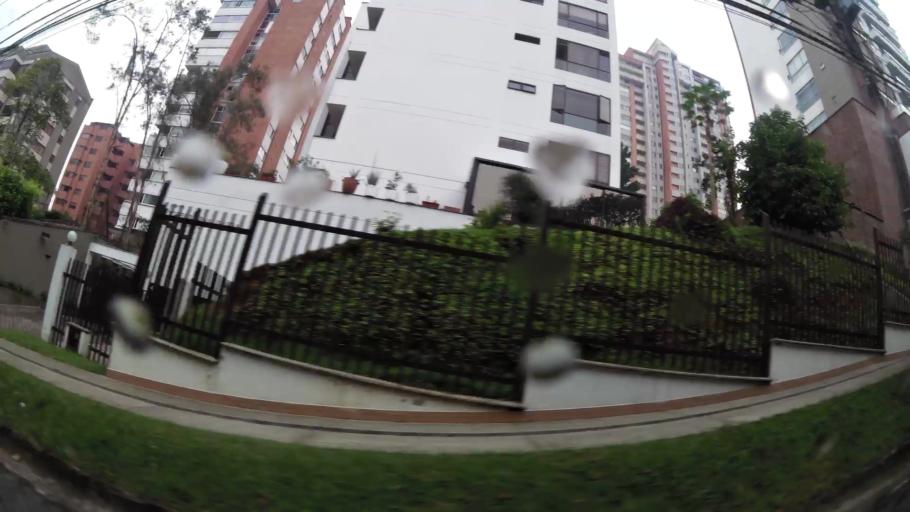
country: CO
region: Antioquia
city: Envigado
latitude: 6.1985
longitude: -75.5711
